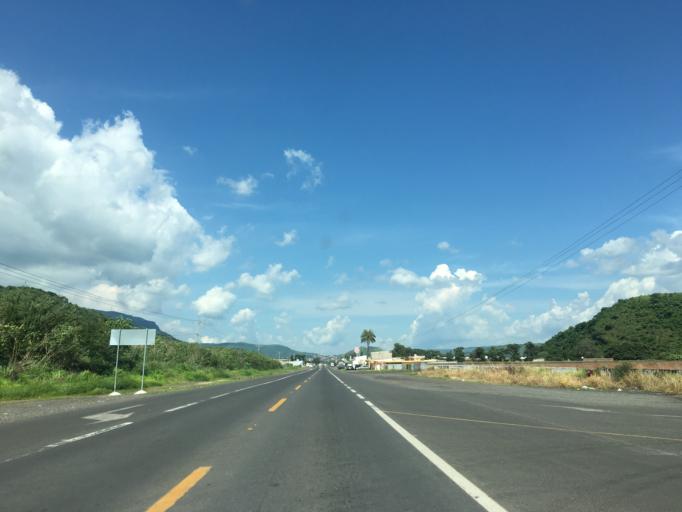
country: MX
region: Nayarit
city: Ixtlan del Rio
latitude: 21.0365
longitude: -104.4049
